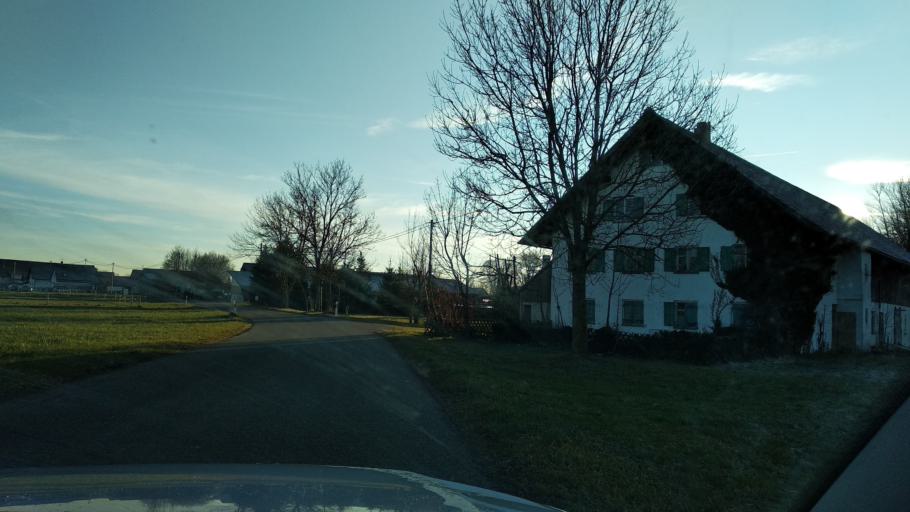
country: DE
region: Bavaria
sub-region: Swabia
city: Lautrach
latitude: 47.9161
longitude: 10.1300
